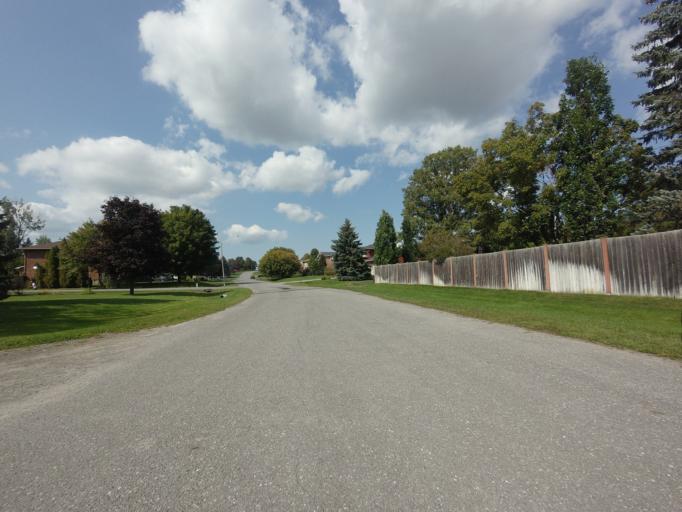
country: CA
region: Ontario
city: Bells Corners
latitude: 45.2377
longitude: -75.6942
